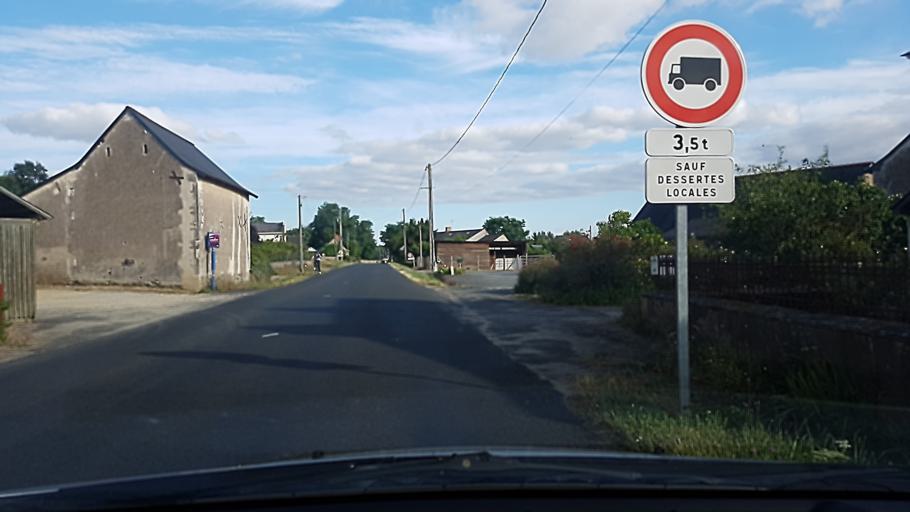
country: FR
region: Pays de la Loire
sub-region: Departement de Maine-et-Loire
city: Maze
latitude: 47.4705
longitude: -0.2829
